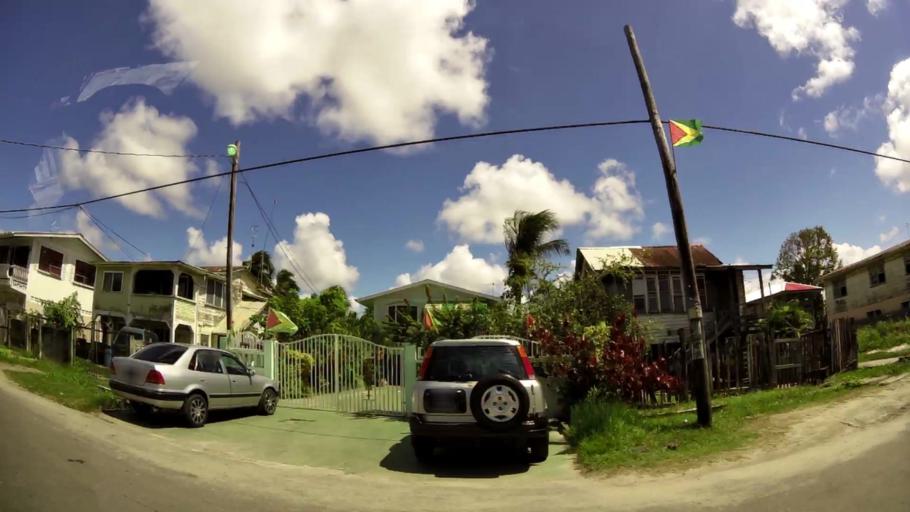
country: GY
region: Demerara-Mahaica
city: Georgetown
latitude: 6.8003
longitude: -58.1428
